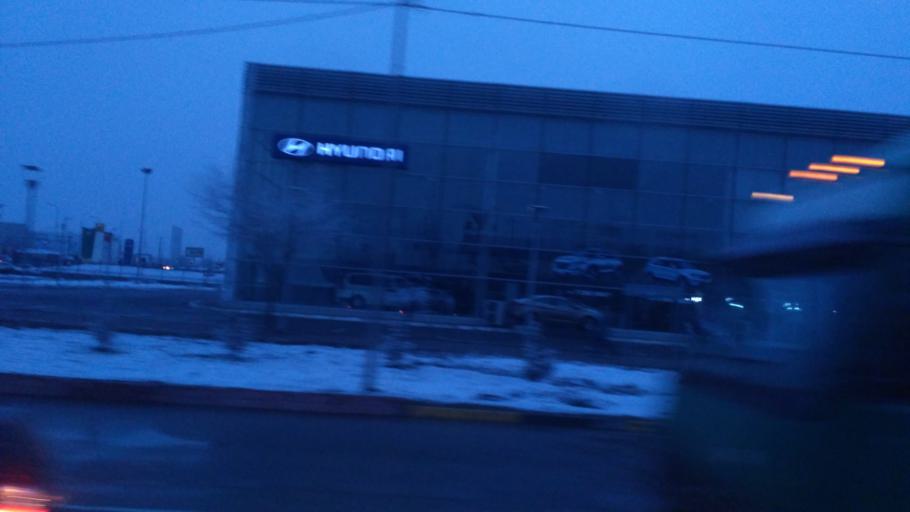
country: KZ
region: Ongtustik Qazaqstan
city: Shymkent
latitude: 42.3517
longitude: 69.5312
